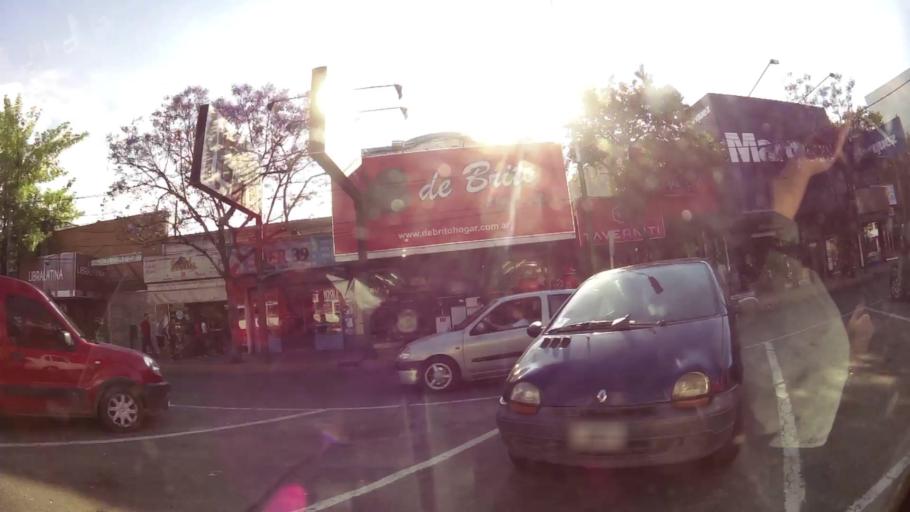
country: AR
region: Buenos Aires
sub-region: Partido de Merlo
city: Merlo
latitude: -34.6680
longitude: -58.7263
